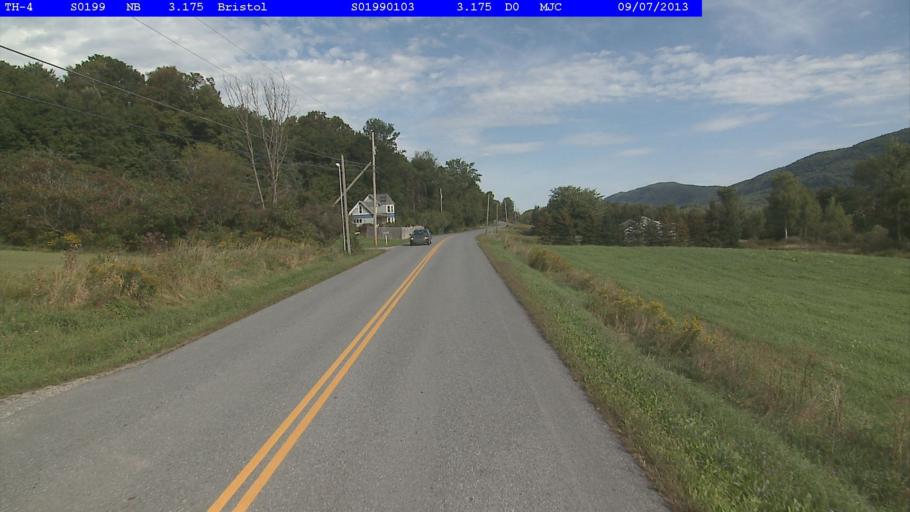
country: US
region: Vermont
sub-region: Addison County
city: Bristol
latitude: 44.1739
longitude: -73.1021
